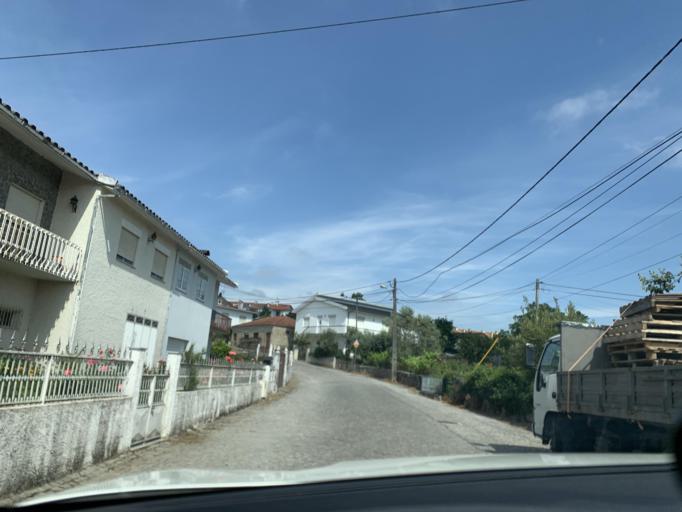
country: PT
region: Viseu
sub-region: Viseu
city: Viseu
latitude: 40.6437
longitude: -7.9012
